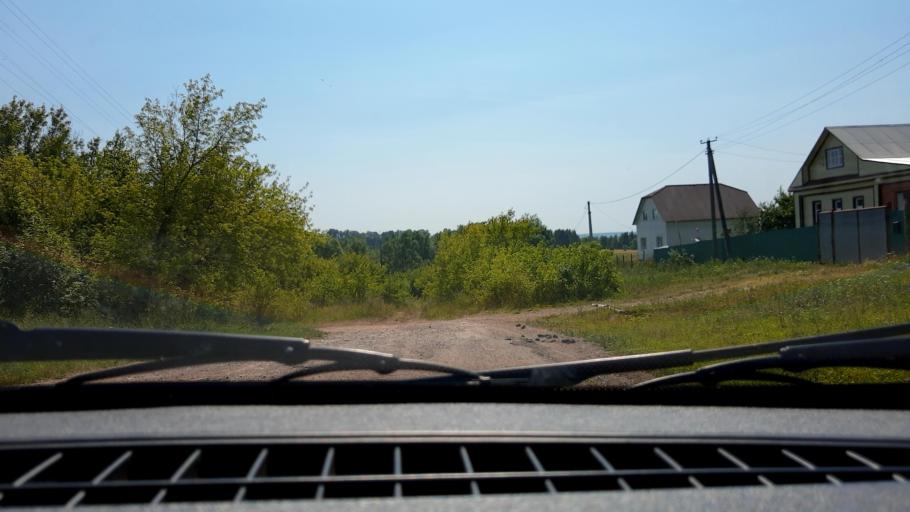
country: RU
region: Bashkortostan
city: Kushnarenkovo
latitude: 55.0696
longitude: 55.1647
